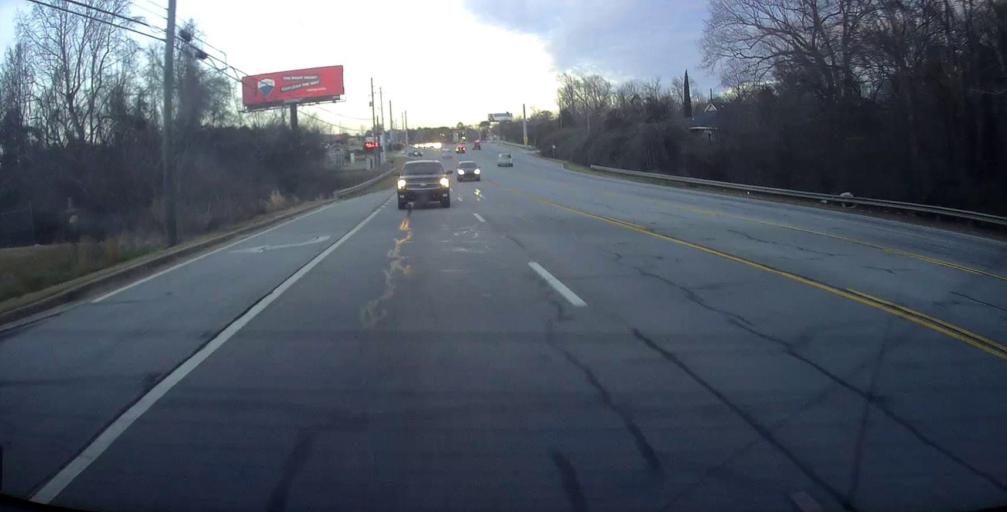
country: US
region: Alabama
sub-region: Russell County
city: Phenix City
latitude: 32.5584
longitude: -84.9425
